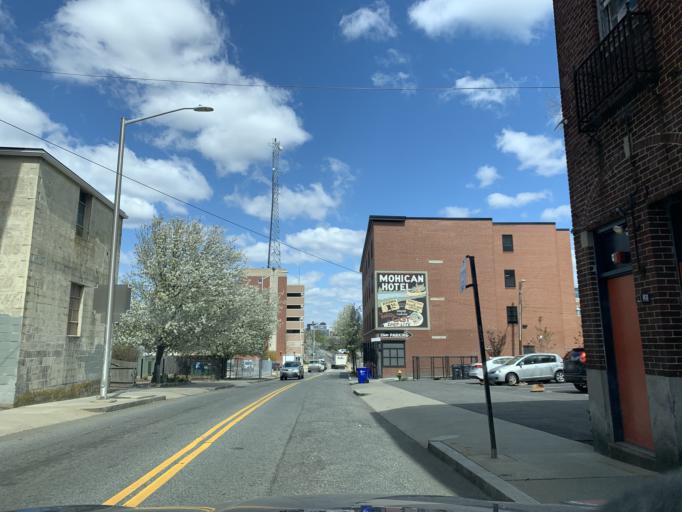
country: US
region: Rhode Island
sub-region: Providence County
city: Providence
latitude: 41.8183
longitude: -71.4202
